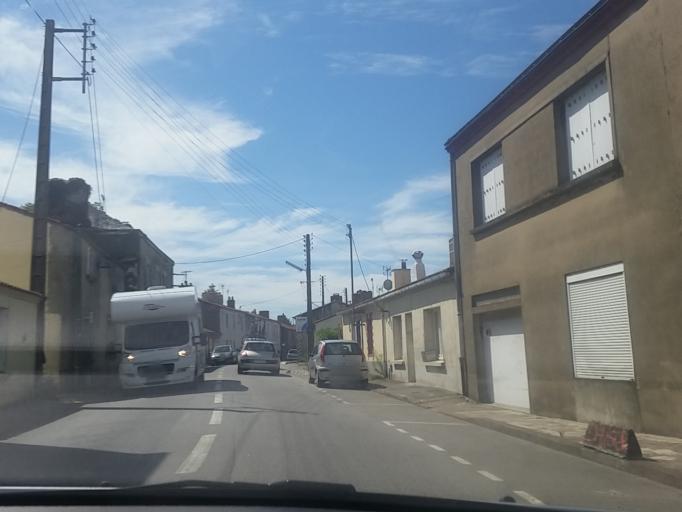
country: FR
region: Pays de la Loire
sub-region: Departement de la Loire-Atlantique
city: Vue
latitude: 47.1988
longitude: -1.8841
